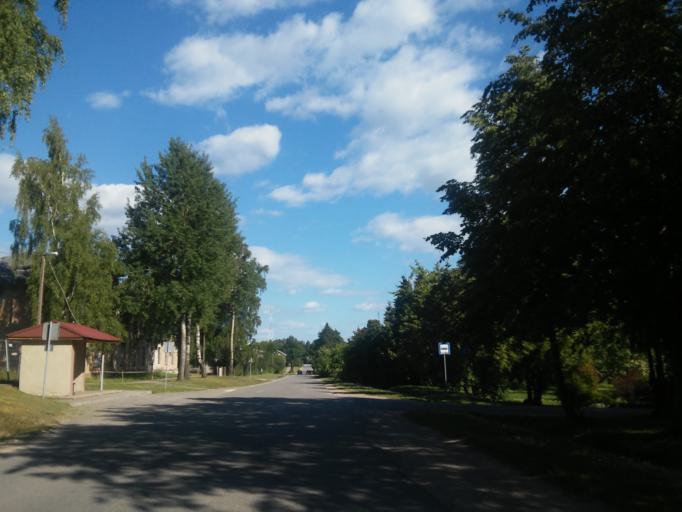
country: LV
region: Vainode
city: Vainode
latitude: 56.4177
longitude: 21.8455
